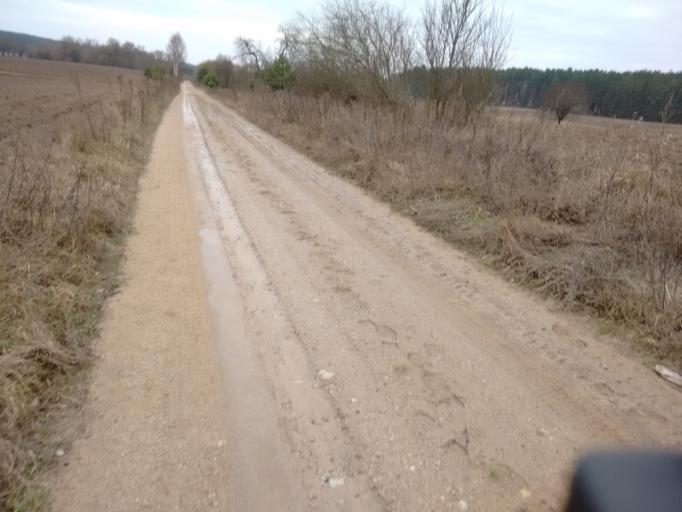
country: LT
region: Alytaus apskritis
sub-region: Alytus
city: Alytus
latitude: 54.2325
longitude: 23.9601
